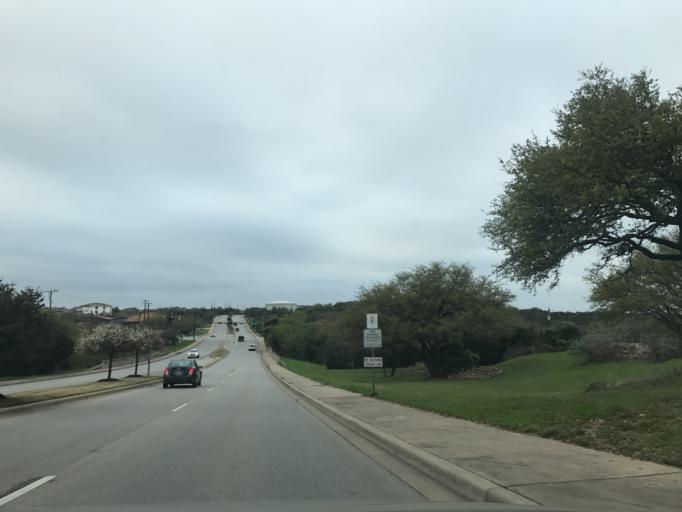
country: US
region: Texas
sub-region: Travis County
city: The Hills
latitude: 30.3420
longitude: -97.9708
